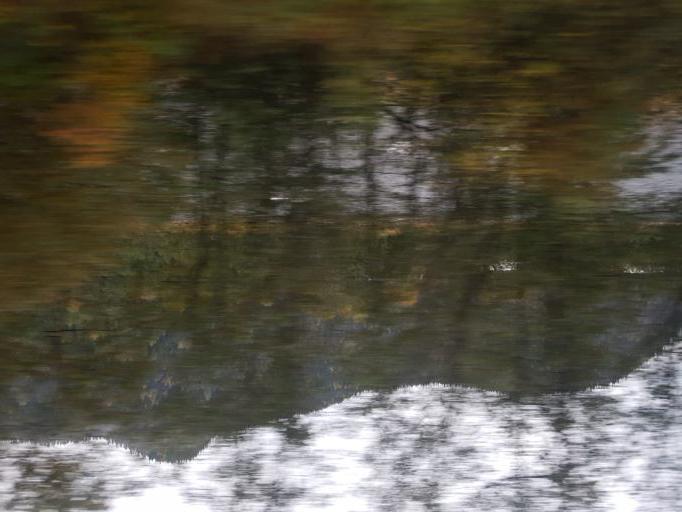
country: NO
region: Sor-Trondelag
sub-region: Midtre Gauldal
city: Storen
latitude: 63.0726
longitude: 10.2701
